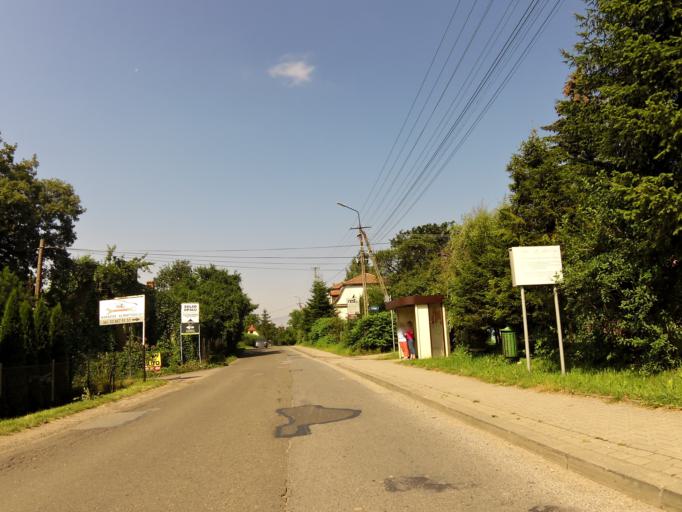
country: PL
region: Silesian Voivodeship
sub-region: Powiat zywiecki
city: Wieprz
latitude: 49.6360
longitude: 19.1733
